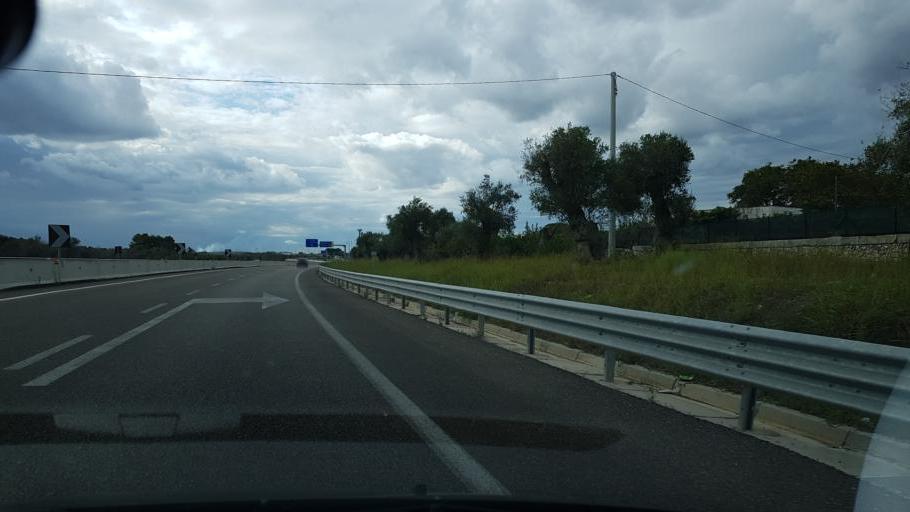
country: IT
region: Apulia
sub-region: Provincia di Lecce
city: Palmariggi
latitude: 40.1264
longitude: 18.3766
